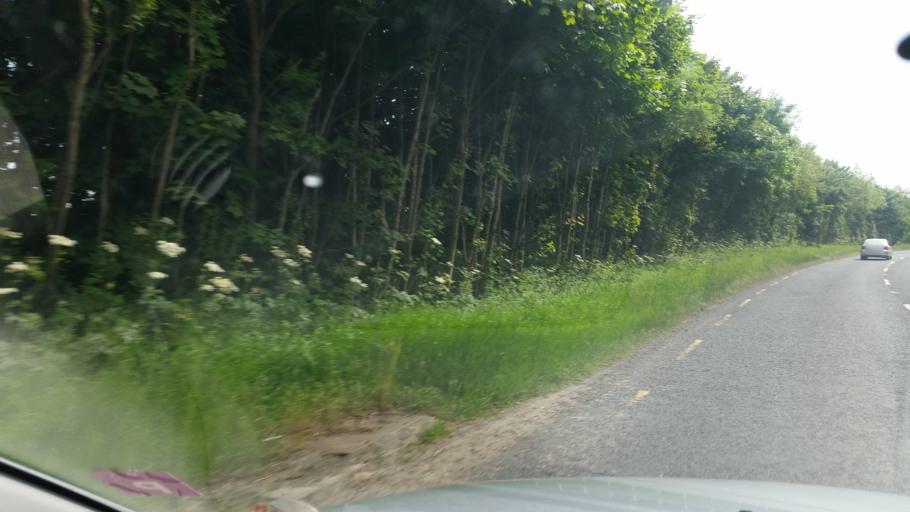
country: IE
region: Leinster
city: Ballymun
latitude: 53.4357
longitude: -6.2927
